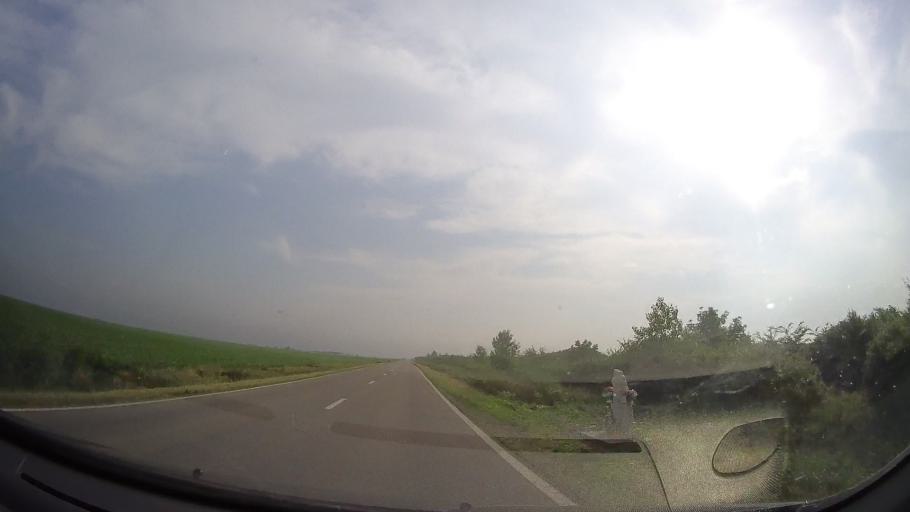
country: RO
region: Timis
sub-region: Comuna Peciu Nou
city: Peciu Nou
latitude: 45.6228
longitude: 21.0869
